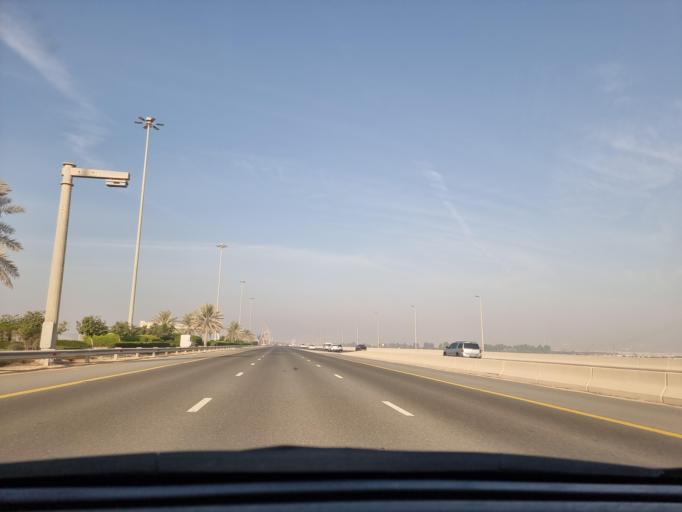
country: AE
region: Abu Dhabi
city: Abu Dhabi
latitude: 24.4873
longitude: 54.6382
